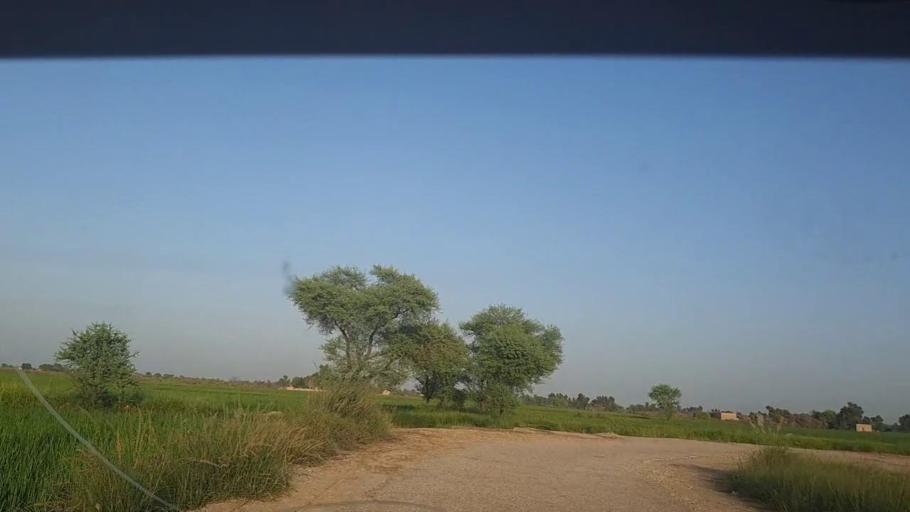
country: PK
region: Sindh
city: Thul
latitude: 28.1260
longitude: 68.8936
